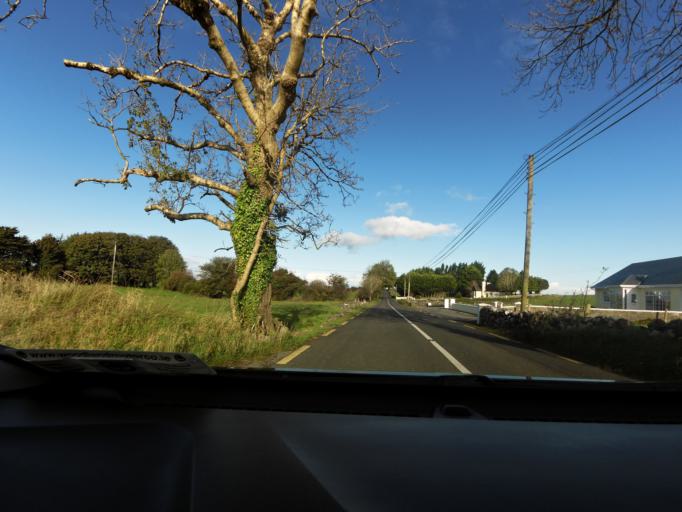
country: IE
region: Connaught
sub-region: Maigh Eo
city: Ballinrobe
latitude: 53.5475
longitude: -9.1043
